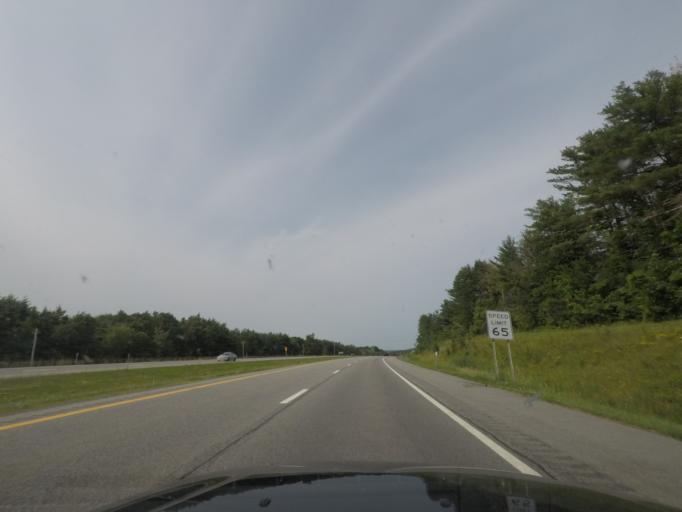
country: US
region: New York
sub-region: Essex County
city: Keeseville
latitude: 44.4527
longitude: -73.4885
